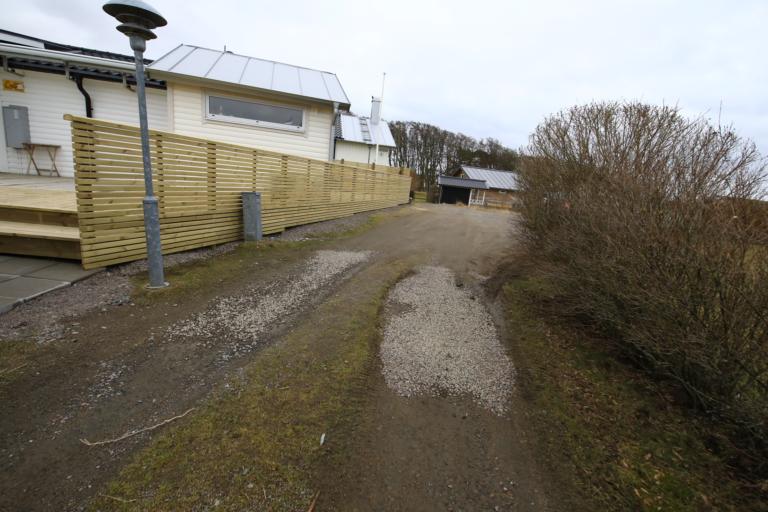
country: SE
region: Halland
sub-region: Varbergs Kommun
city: Traslovslage
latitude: 57.0684
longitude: 12.2798
